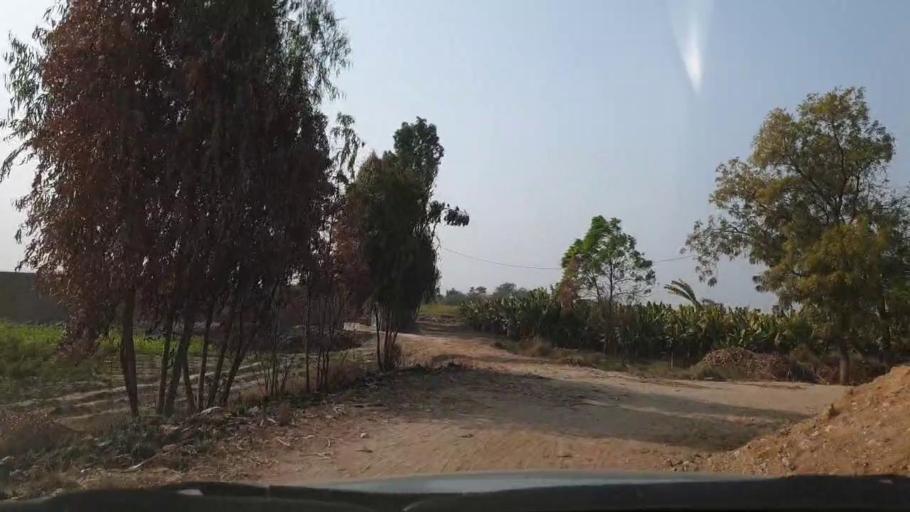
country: PK
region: Sindh
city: Matiari
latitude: 25.6198
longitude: 68.5662
